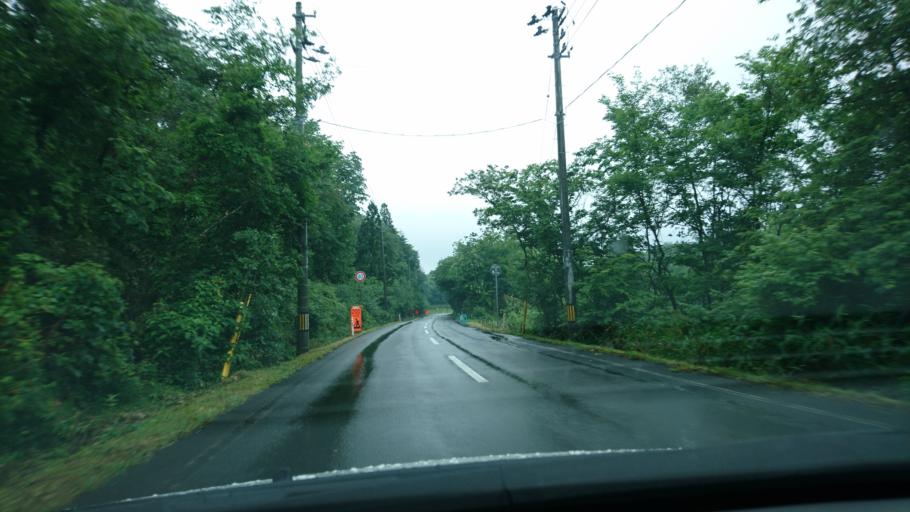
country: JP
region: Iwate
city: Ichinoseki
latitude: 38.9167
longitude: 141.0283
